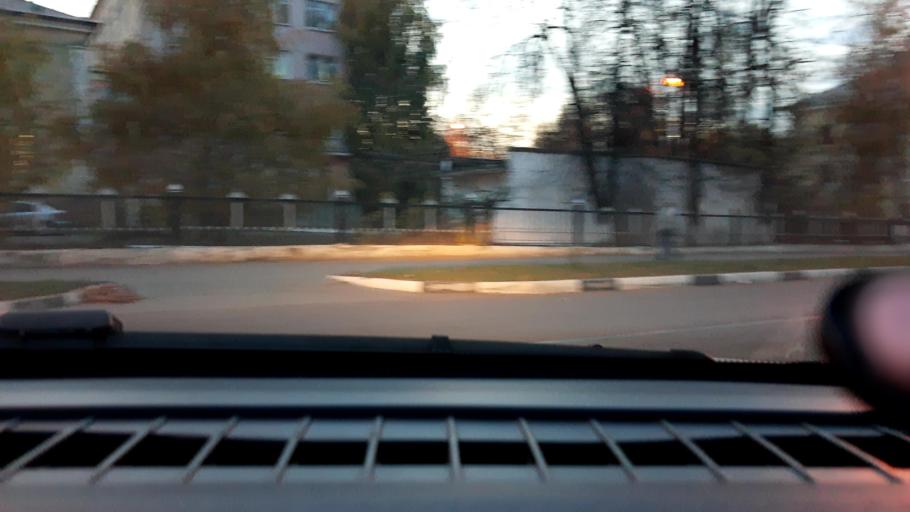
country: RU
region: Nizjnij Novgorod
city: Gorbatovka
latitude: 56.3302
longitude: 43.8532
